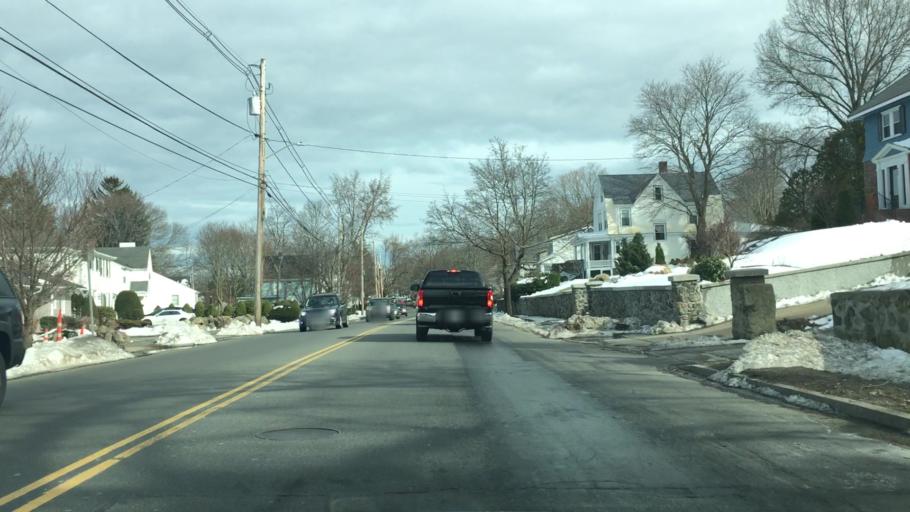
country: US
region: Massachusetts
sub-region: Essex County
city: Peabody
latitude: 42.5333
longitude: -70.9490
